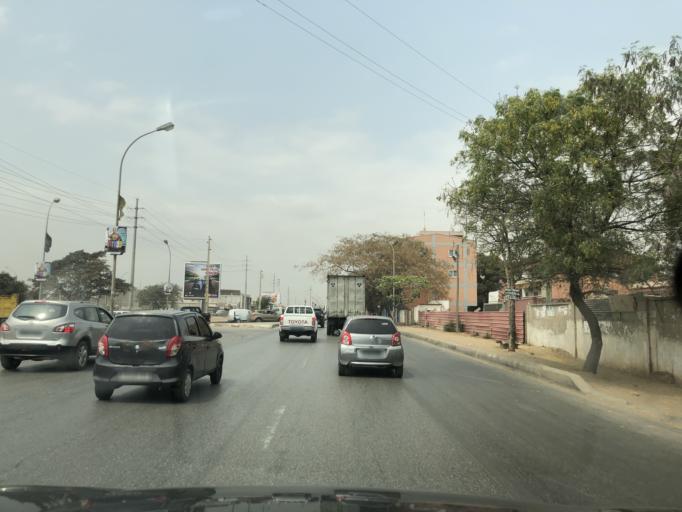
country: AO
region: Luanda
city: Luanda
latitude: -8.9003
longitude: 13.2089
